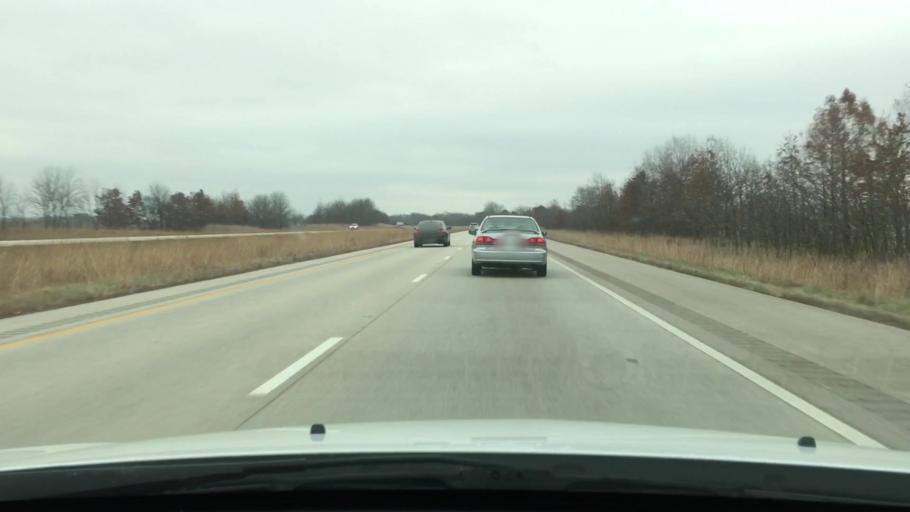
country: US
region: Illinois
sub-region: Sangamon County
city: New Berlin
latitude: 39.7411
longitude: -89.8339
